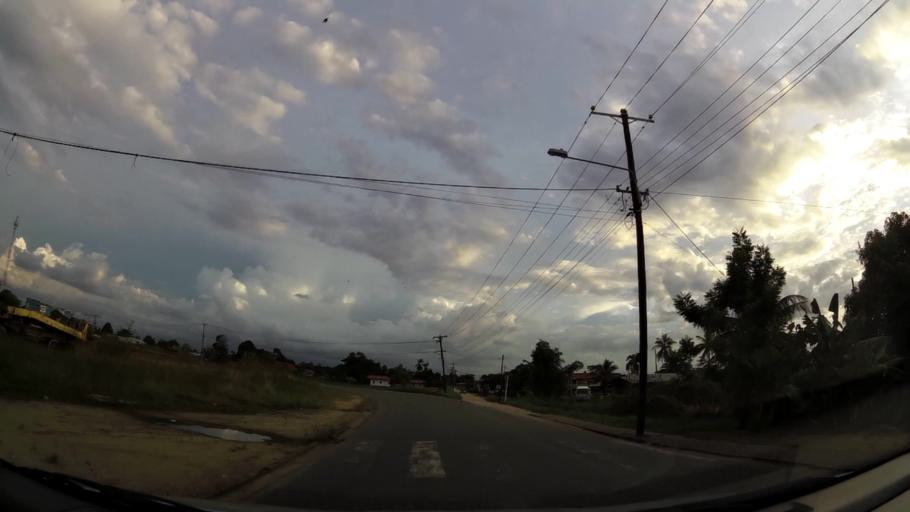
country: SR
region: Paramaribo
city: Paramaribo
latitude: 5.7777
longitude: -55.1676
